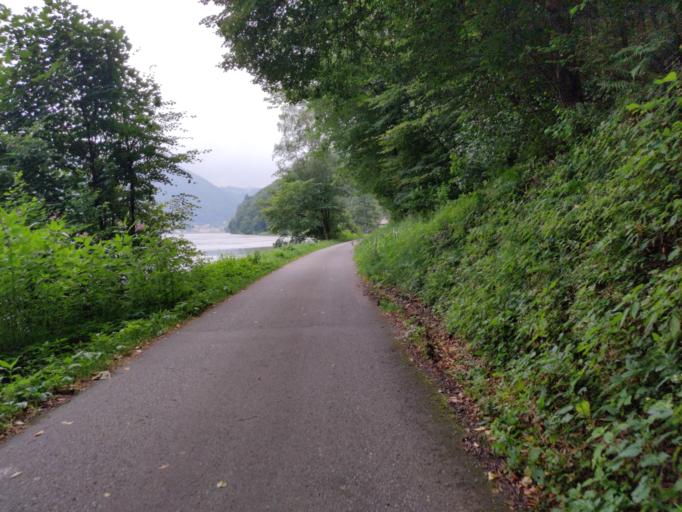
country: AT
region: Lower Austria
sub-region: Politischer Bezirk Melk
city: Nochling
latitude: 48.2319
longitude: 14.9167
